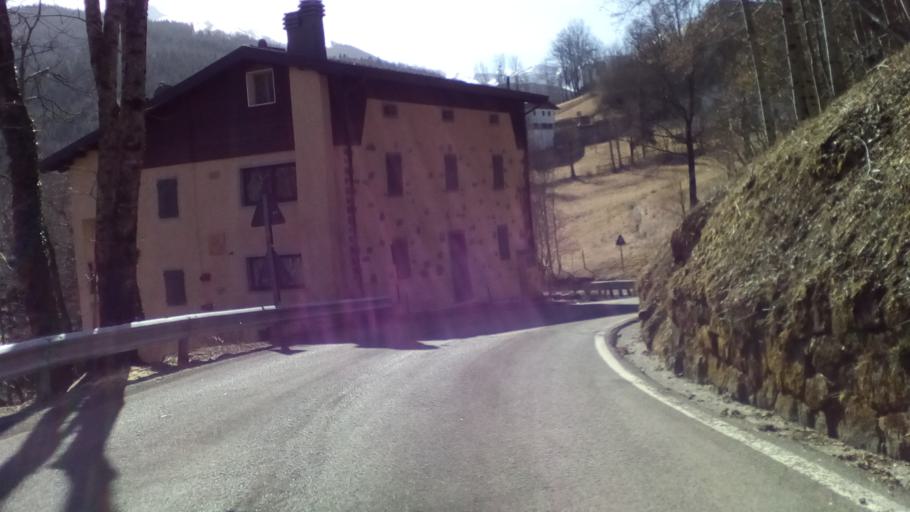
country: IT
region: Emilia-Romagna
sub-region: Provincia di Modena
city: Pievepelago
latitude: 44.1889
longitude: 10.5618
